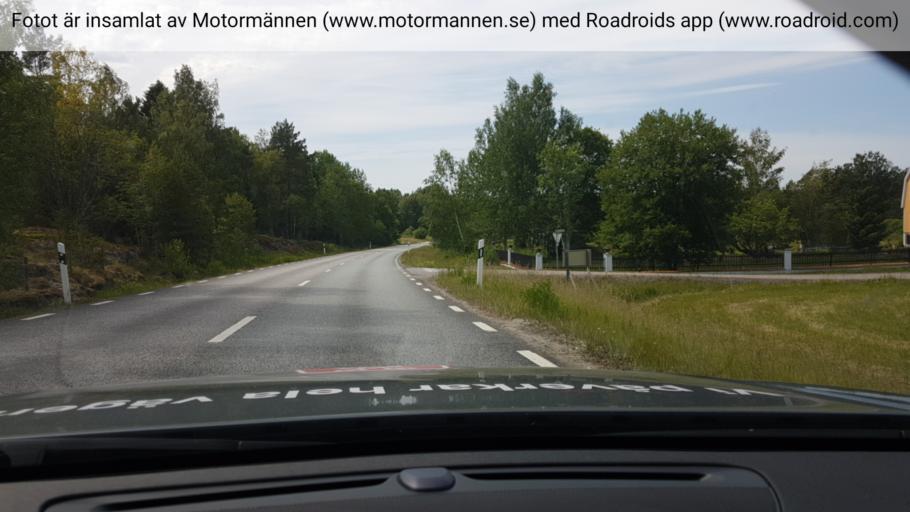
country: SE
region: Uppsala
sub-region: Osthammars Kommun
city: Marieberg
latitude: 60.1639
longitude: 18.4621
